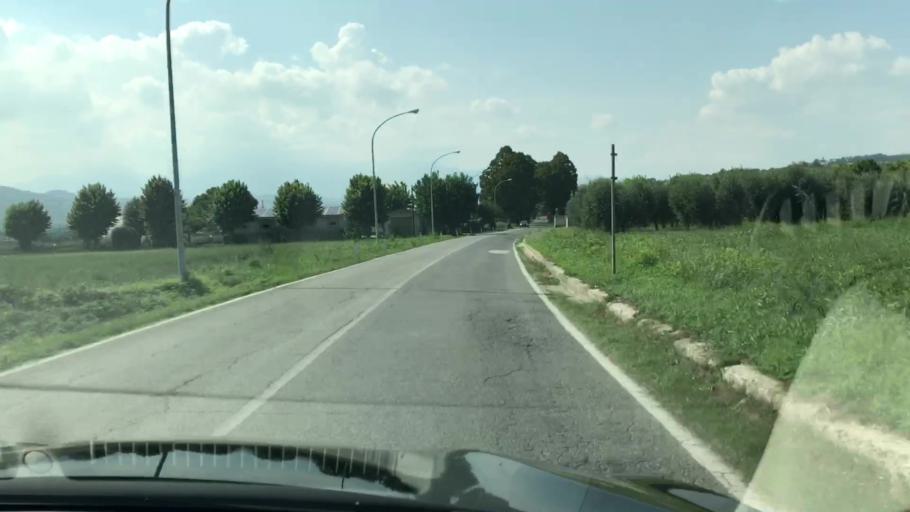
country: IT
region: The Marches
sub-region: Provincia di Ascoli Piceno
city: Monsampolo del Tronto
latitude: 42.8798
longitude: 13.7871
